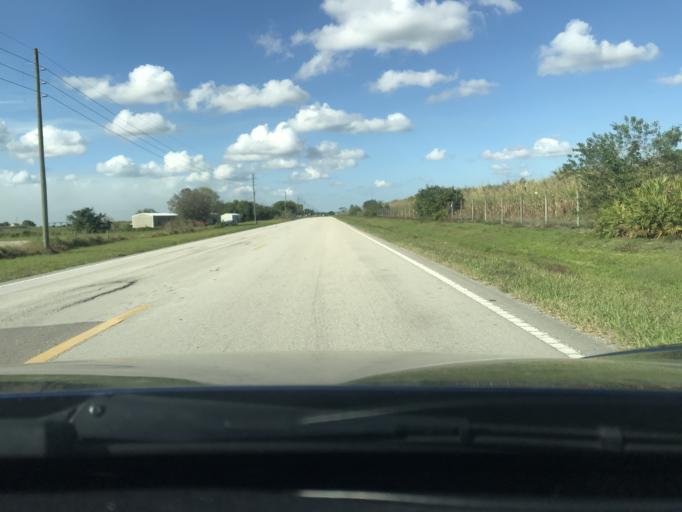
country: US
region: Florida
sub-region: Okeechobee County
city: Taylor Creek
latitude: 27.2620
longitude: -80.6946
